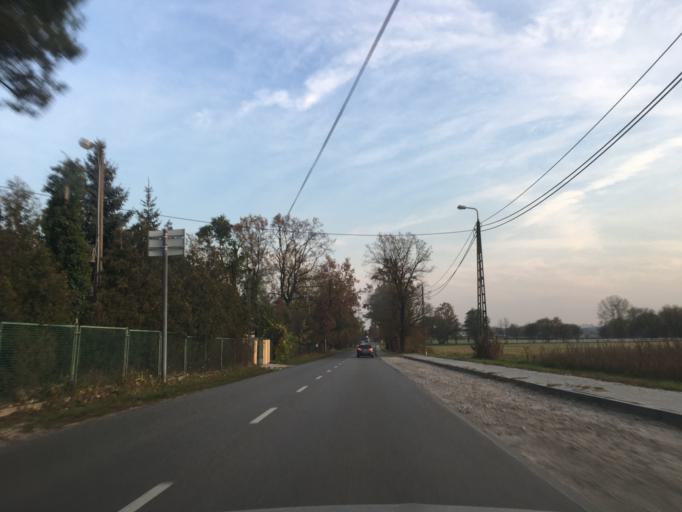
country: PL
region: Masovian Voivodeship
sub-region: Powiat piaseczynski
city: Lesznowola
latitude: 52.0576
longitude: 20.9213
